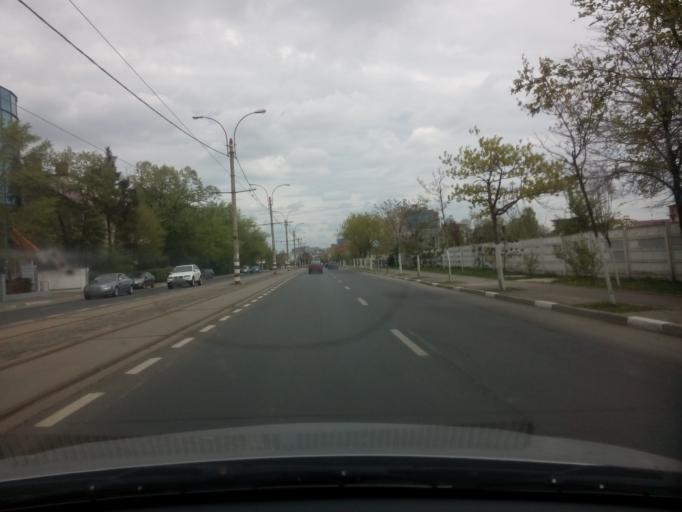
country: RO
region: Bucuresti
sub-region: Municipiul Bucuresti
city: Bucharest
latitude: 44.4671
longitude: 26.1091
